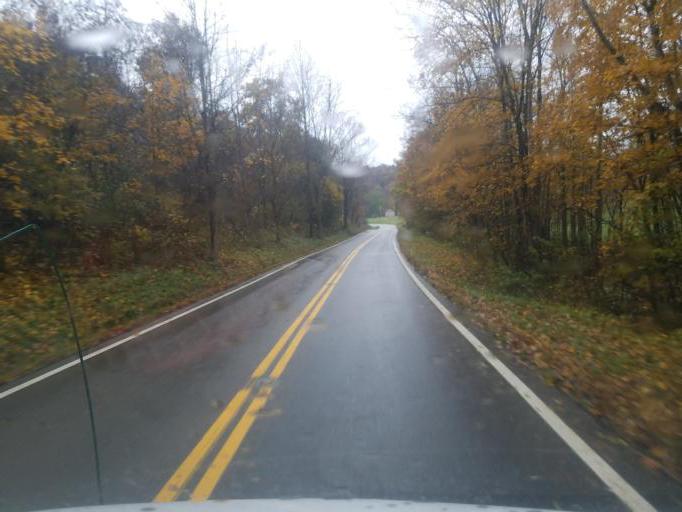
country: US
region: Ohio
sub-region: Washington County
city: Beverly
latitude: 39.4752
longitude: -81.7282
